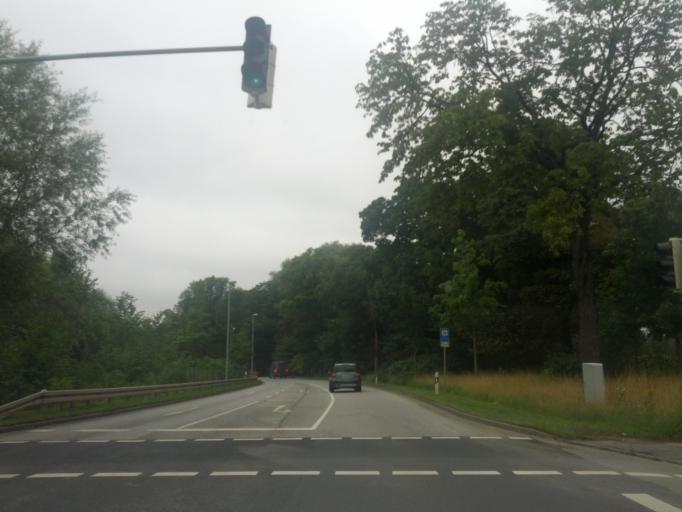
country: DE
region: Mecklenburg-Vorpommern
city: Hornstorf
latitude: 53.8913
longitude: 11.5218
